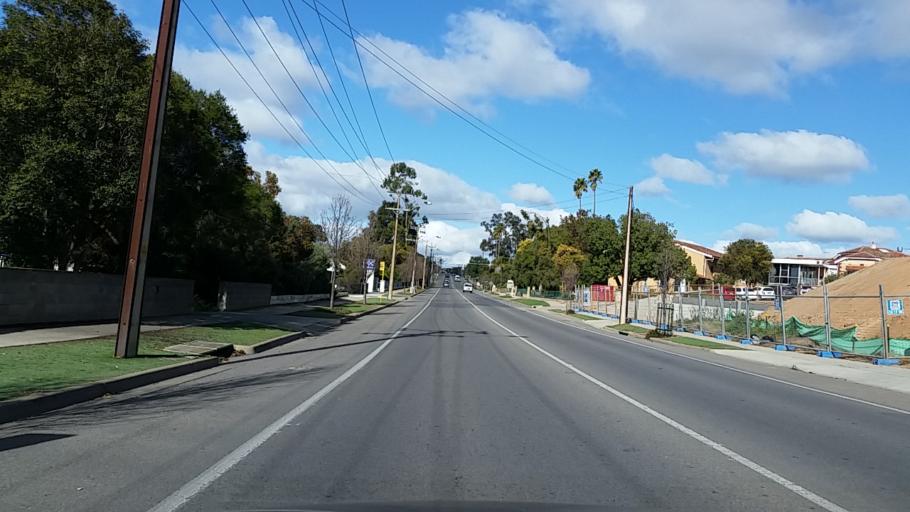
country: AU
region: South Australia
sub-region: Murray Bridge
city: Murray Bridge
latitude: -35.1240
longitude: 139.2764
